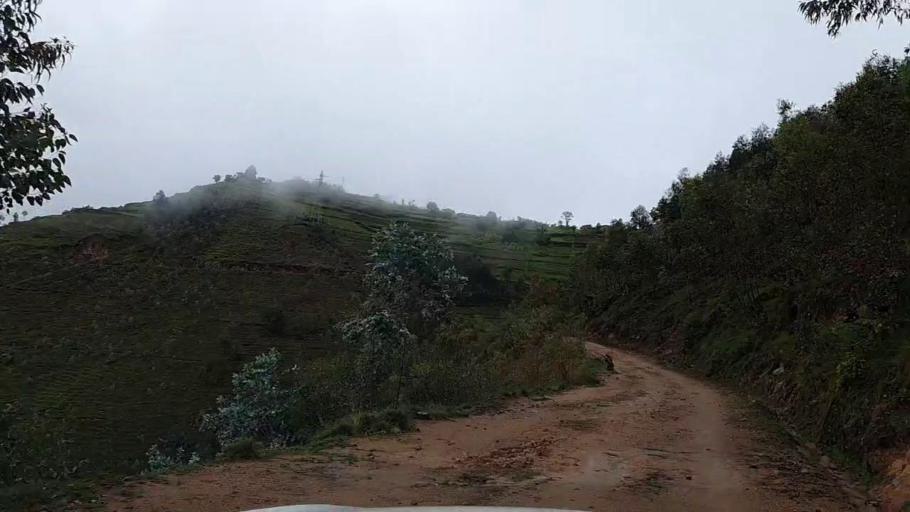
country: RW
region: Southern Province
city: Nzega
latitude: -2.4083
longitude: 29.4910
